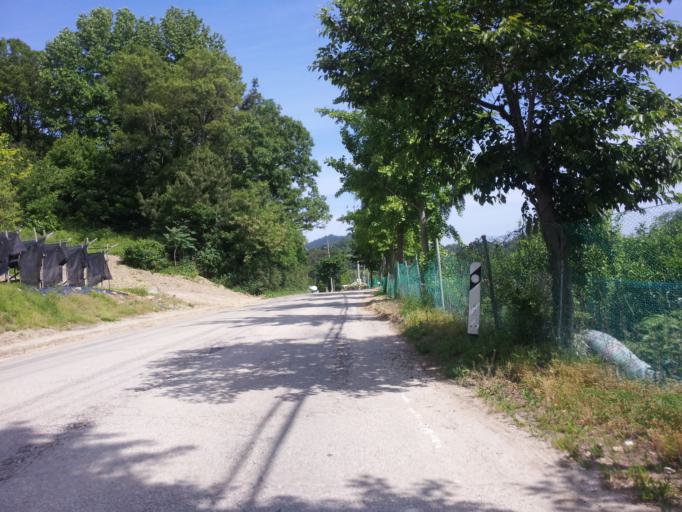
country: KR
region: Daejeon
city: Daejeon
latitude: 36.3413
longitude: 127.4785
